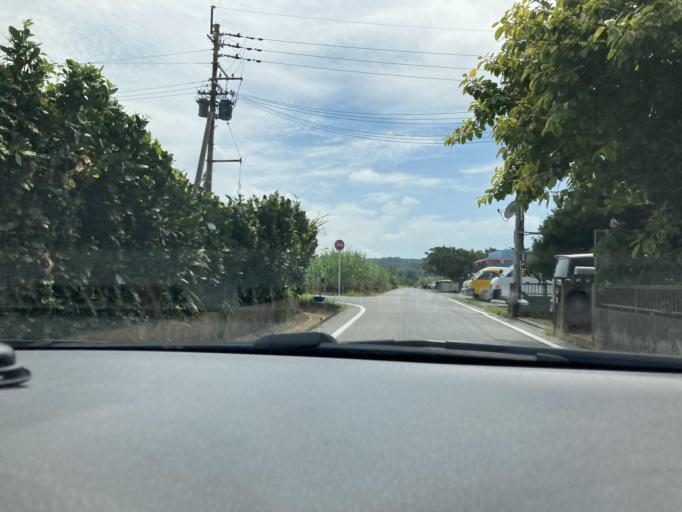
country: JP
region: Okinawa
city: Ishikawa
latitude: 26.4412
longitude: 127.7732
